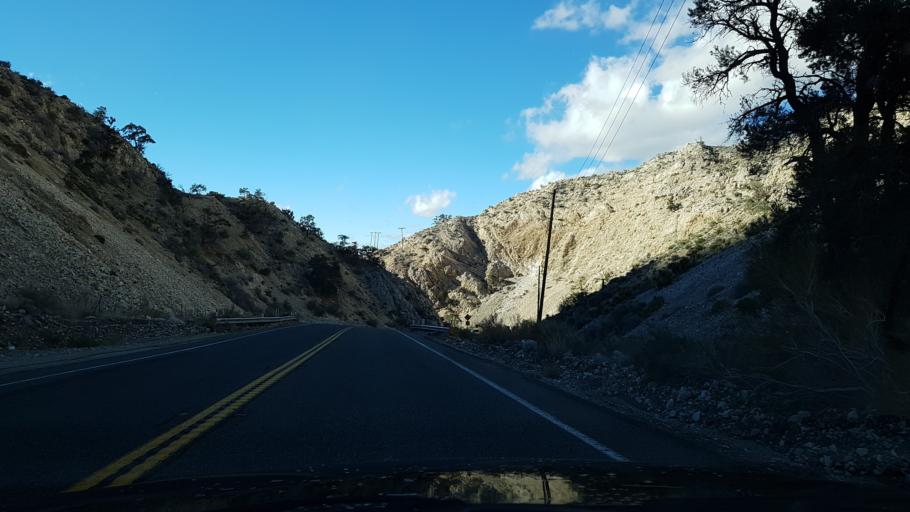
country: US
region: California
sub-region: San Bernardino County
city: Big Bear City
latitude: 34.3461
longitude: -116.8428
